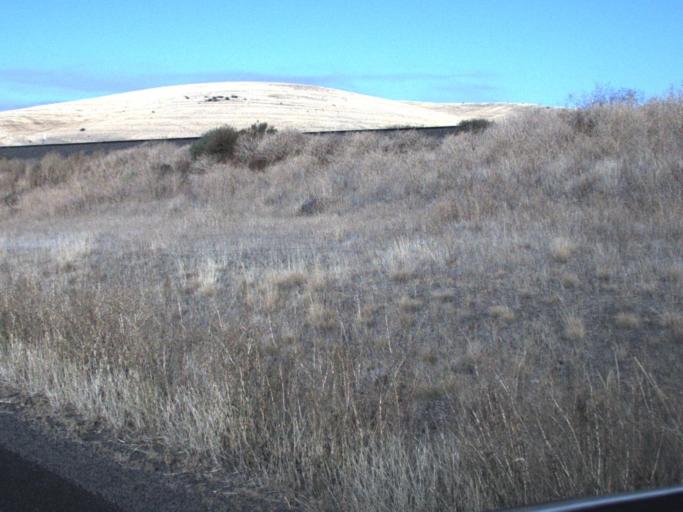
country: US
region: Washington
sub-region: Walla Walla County
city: Walla Walla
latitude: 46.1581
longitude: -118.3793
